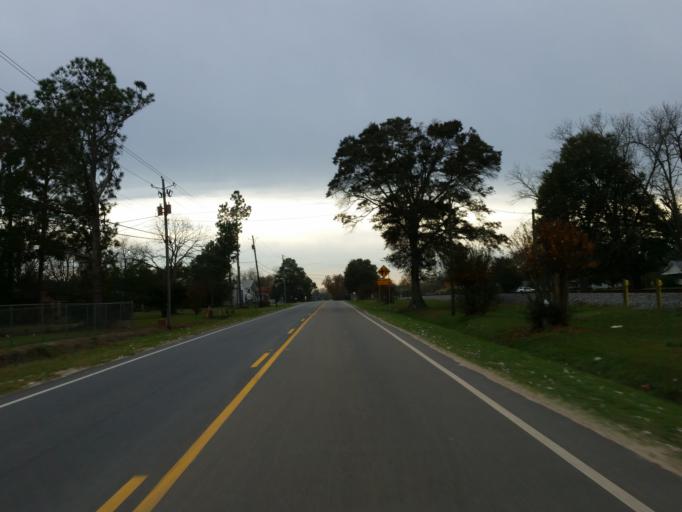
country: US
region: Georgia
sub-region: Turner County
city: Ashburn
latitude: 31.6779
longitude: -83.6394
